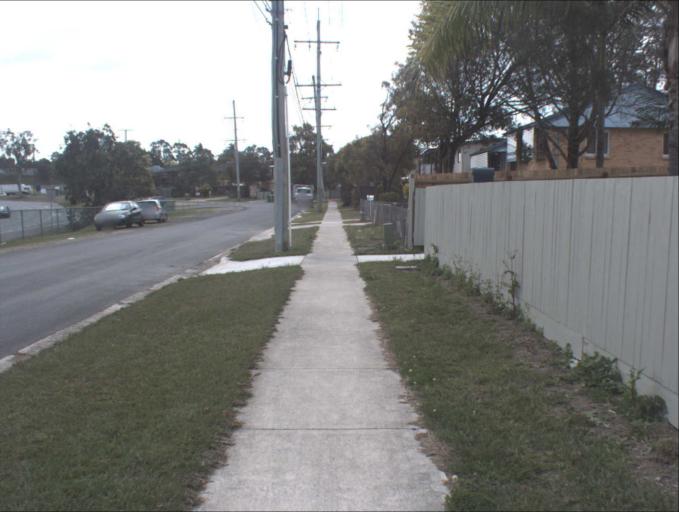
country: AU
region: Queensland
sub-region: Logan
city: Waterford West
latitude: -27.6713
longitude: 153.1227
